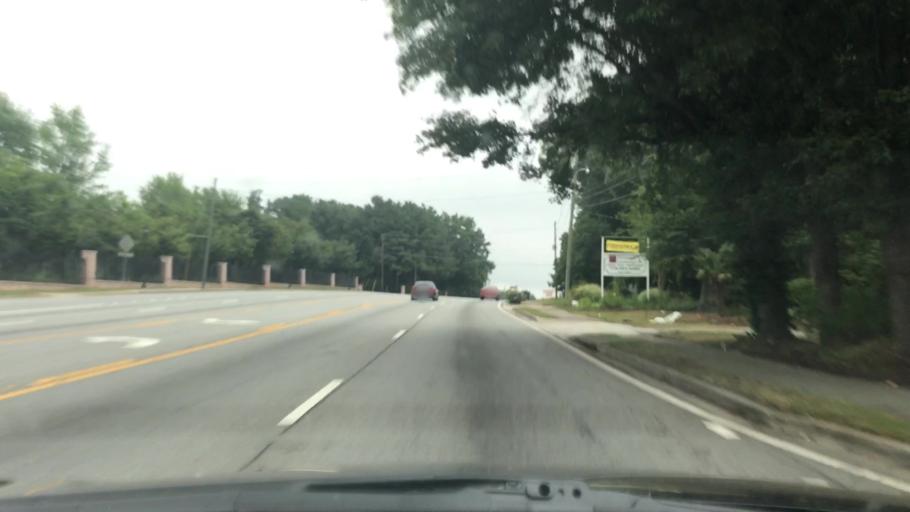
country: US
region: Georgia
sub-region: Gwinnett County
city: Lilburn
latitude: 33.8836
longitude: -84.1610
